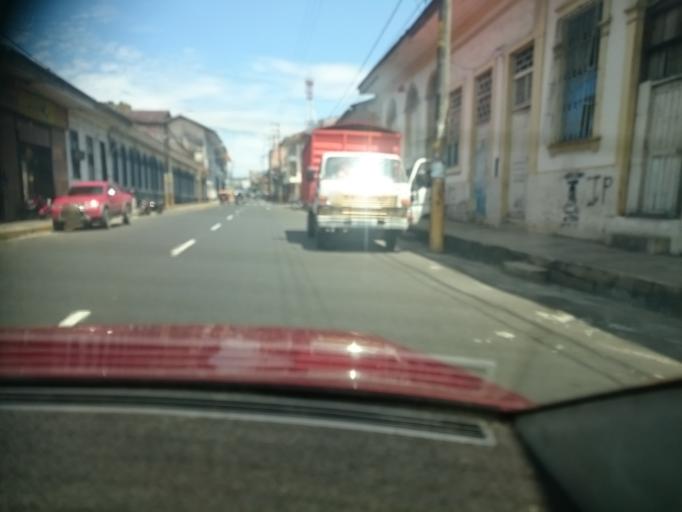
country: PE
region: Loreto
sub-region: Provincia de Maynas
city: Iquitos
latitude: -3.7488
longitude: -73.2460
